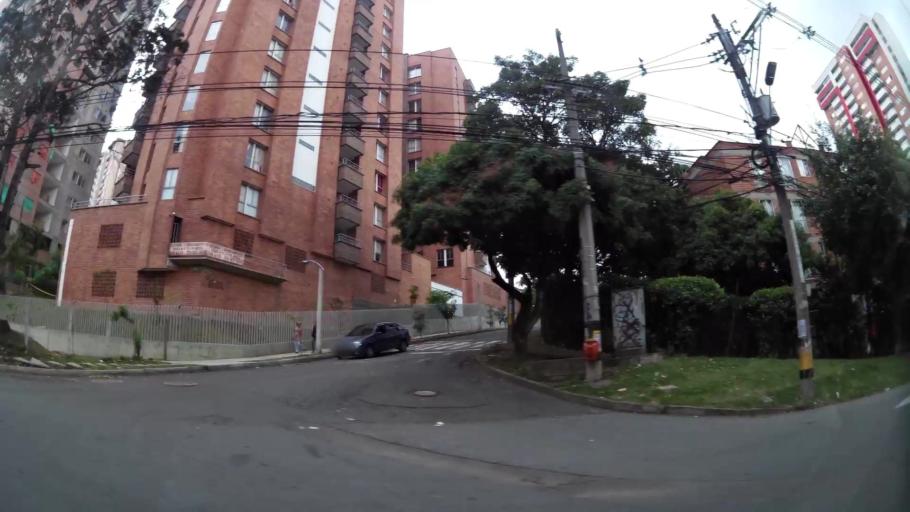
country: CO
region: Antioquia
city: Medellin
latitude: 6.2757
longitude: -75.5846
